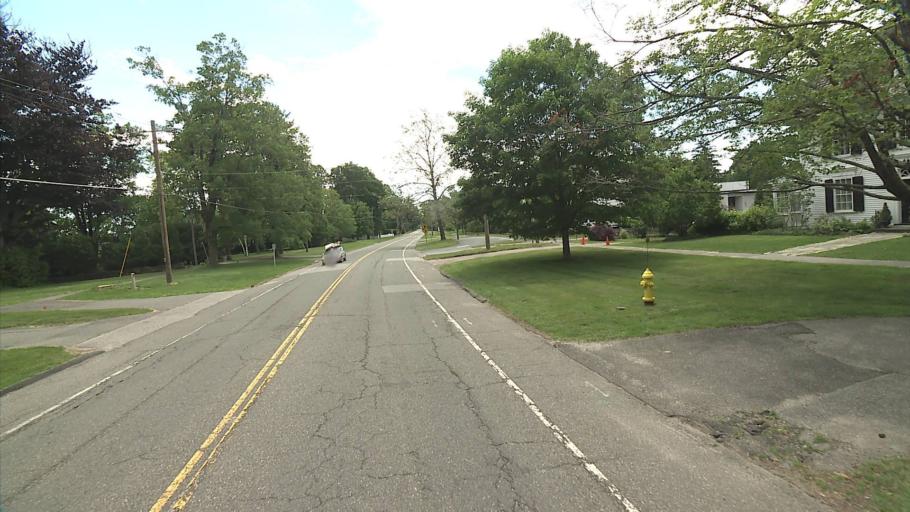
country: US
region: Connecticut
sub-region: Litchfield County
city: Litchfield
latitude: 41.7420
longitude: -73.1874
